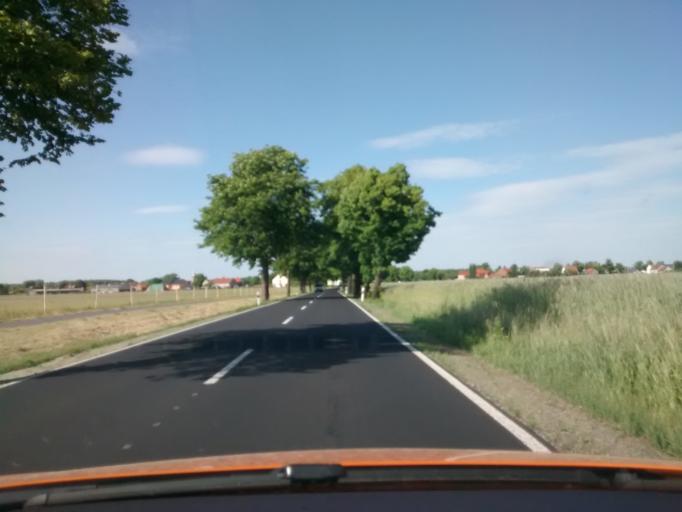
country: DE
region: Brandenburg
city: Trebbin
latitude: 52.2462
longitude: 13.2371
